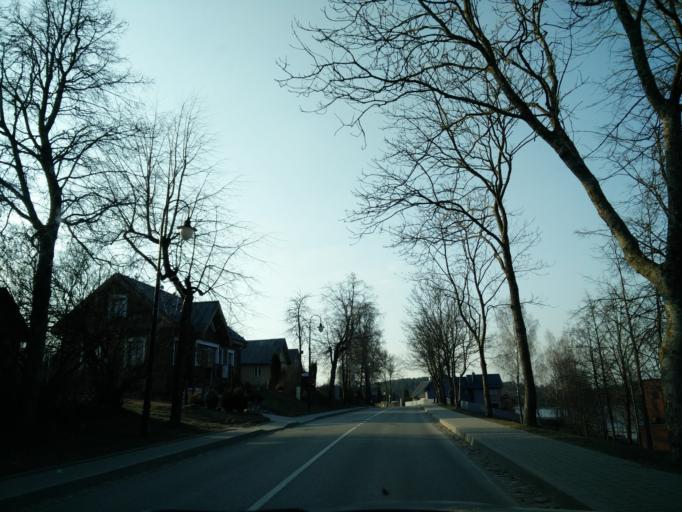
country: LT
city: Trakai
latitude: 54.6514
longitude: 24.9226
